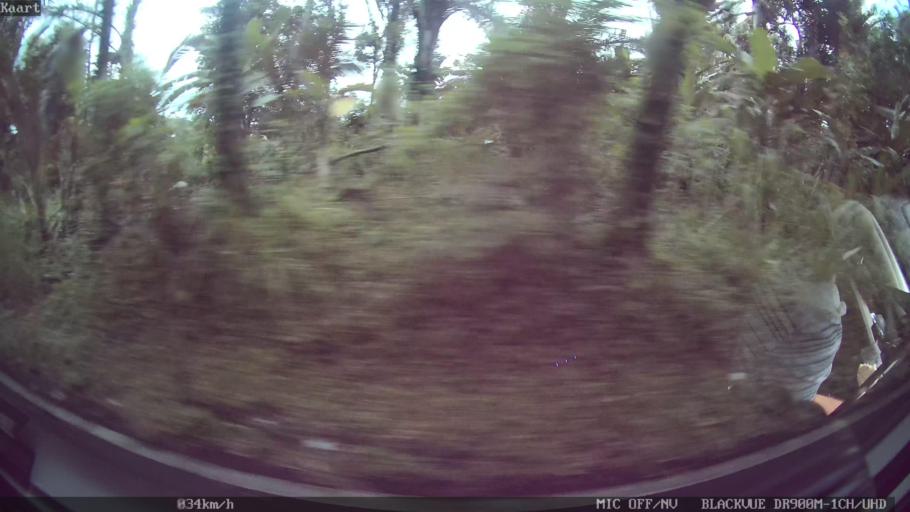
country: ID
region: Bali
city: Pemijian
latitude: -8.4467
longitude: 115.2279
